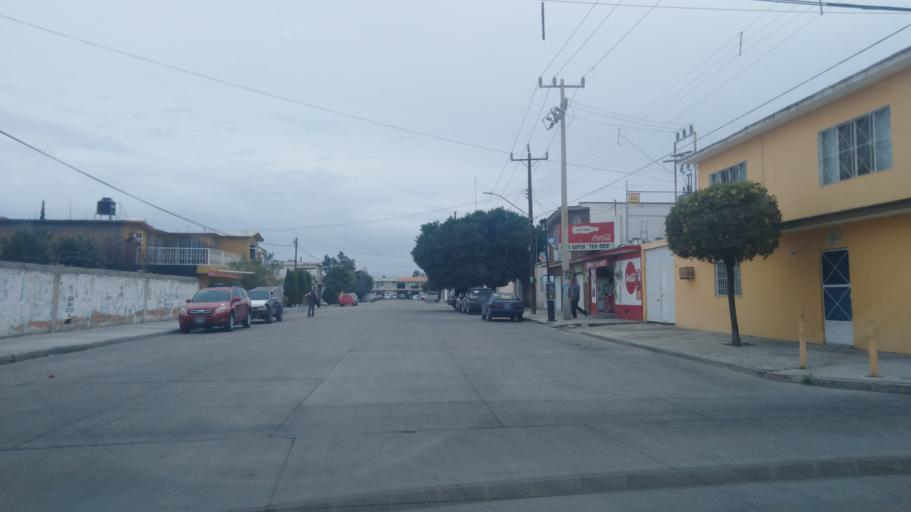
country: MX
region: Durango
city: Victoria de Durango
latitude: 24.0290
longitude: -104.6263
